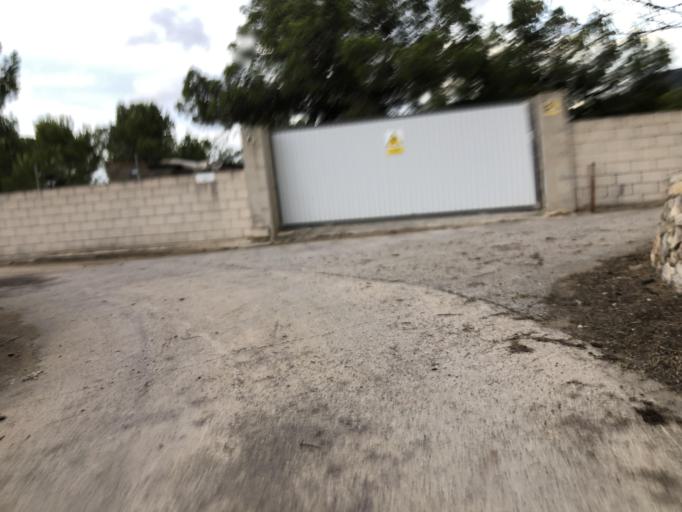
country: ES
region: Valencia
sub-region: Provincia de Alicante
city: Polop
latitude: 38.6363
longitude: -0.1424
